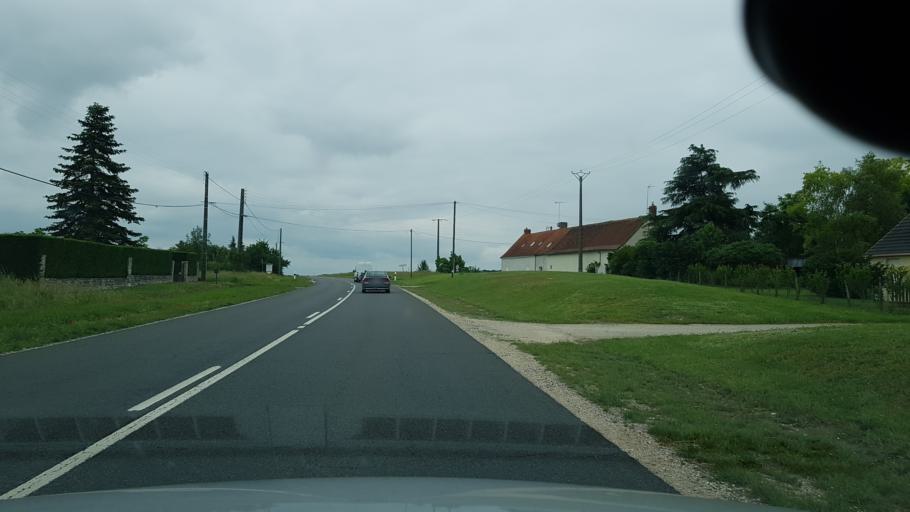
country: FR
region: Centre
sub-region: Departement du Loir-et-Cher
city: Chatillon-sur-Cher
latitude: 47.3028
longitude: 1.5099
